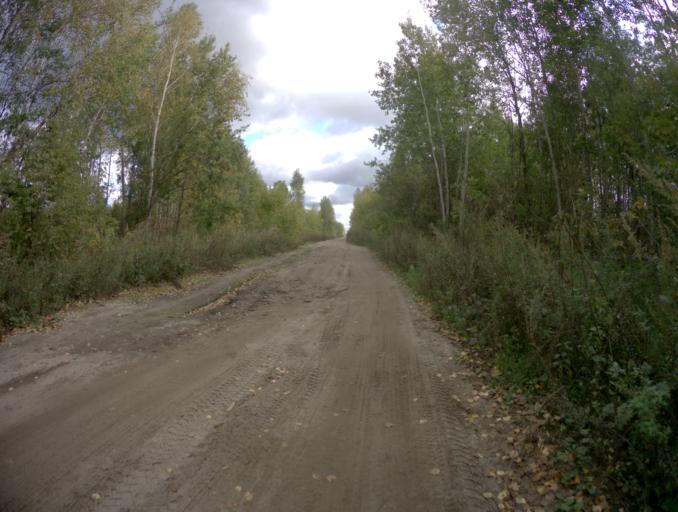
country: RU
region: Moskovskaya
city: Baksheyevo
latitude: 55.7118
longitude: 39.8897
